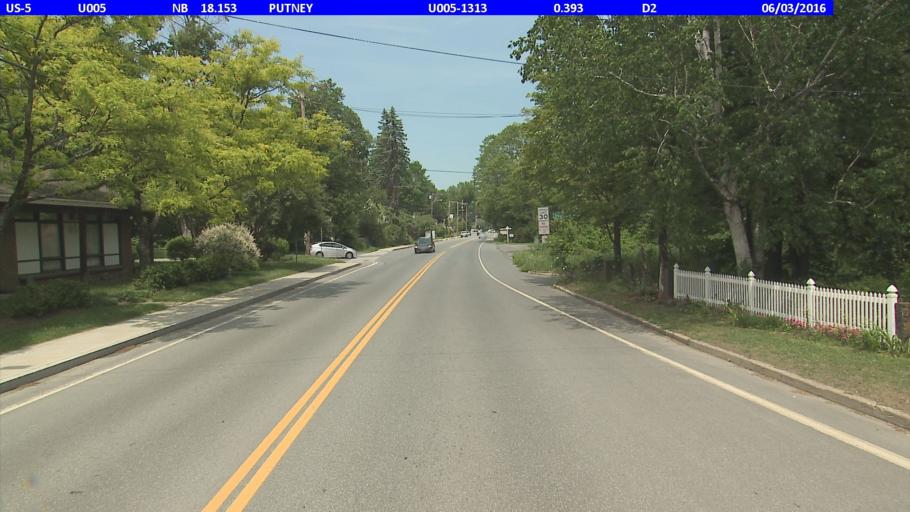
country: US
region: New Hampshire
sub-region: Cheshire County
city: Westmoreland
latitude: 42.9712
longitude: -72.5222
